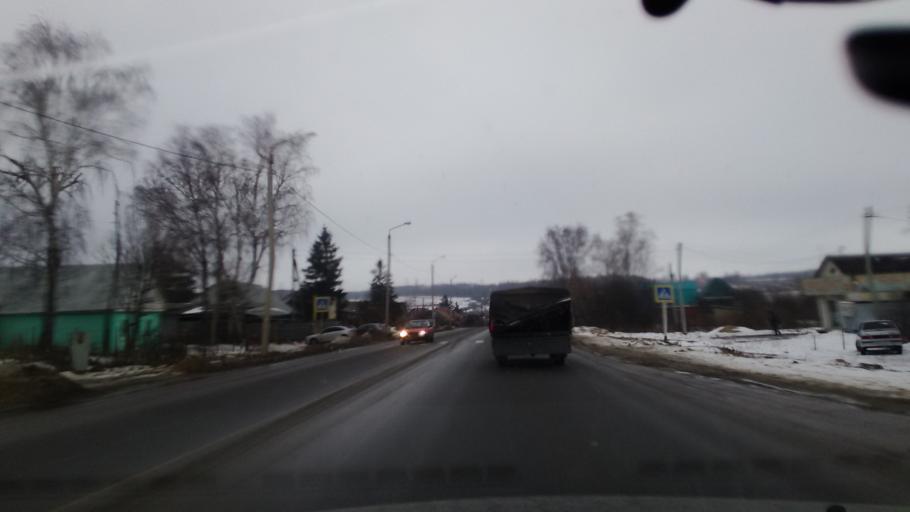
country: RU
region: Tula
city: Skuratovskiy
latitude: 54.1368
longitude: 37.6765
